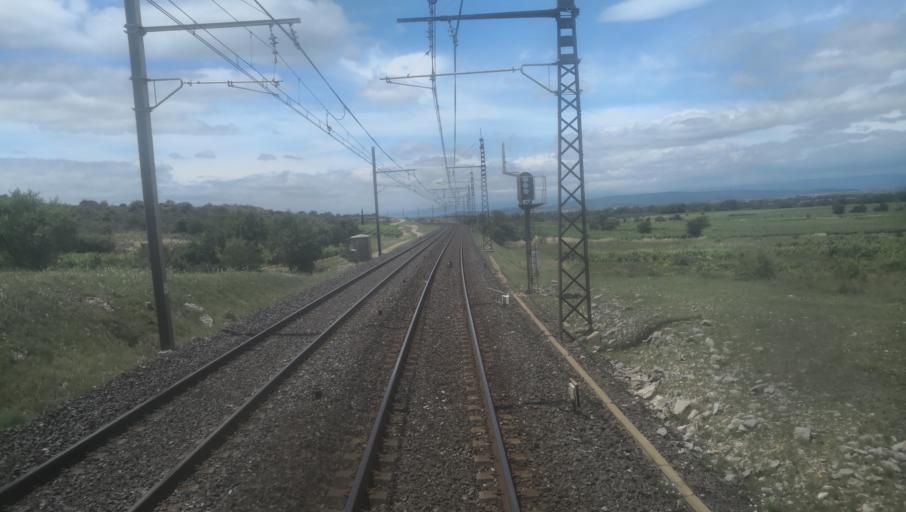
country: FR
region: Languedoc-Roussillon
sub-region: Departement de l'Aude
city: Nevian
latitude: 43.2110
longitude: 2.8957
